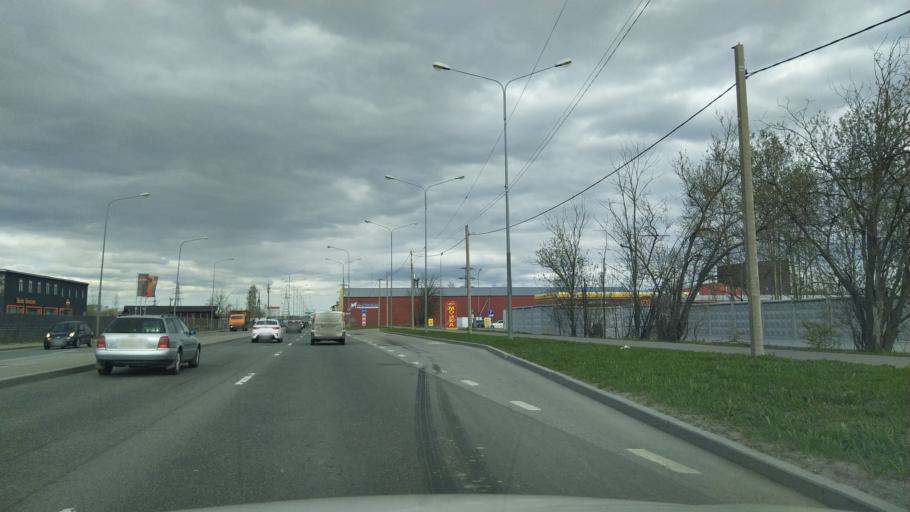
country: RU
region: Leningrad
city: Murino
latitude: 60.0083
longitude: 30.4510
